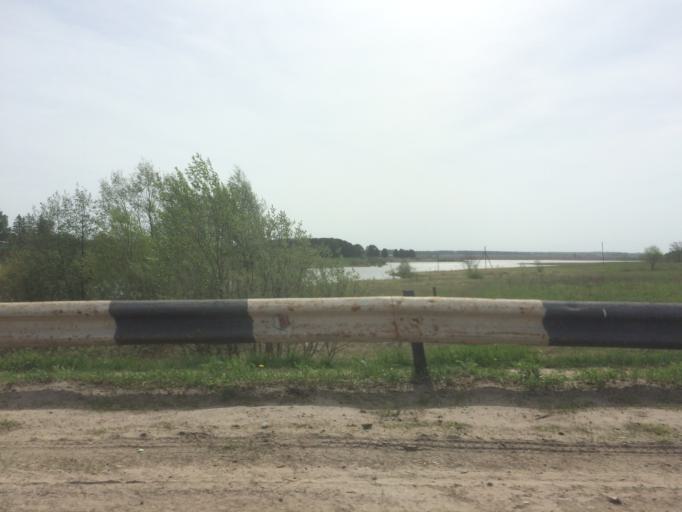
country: RU
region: Mariy-El
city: Sovetskiy
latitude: 56.7756
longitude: 48.6472
